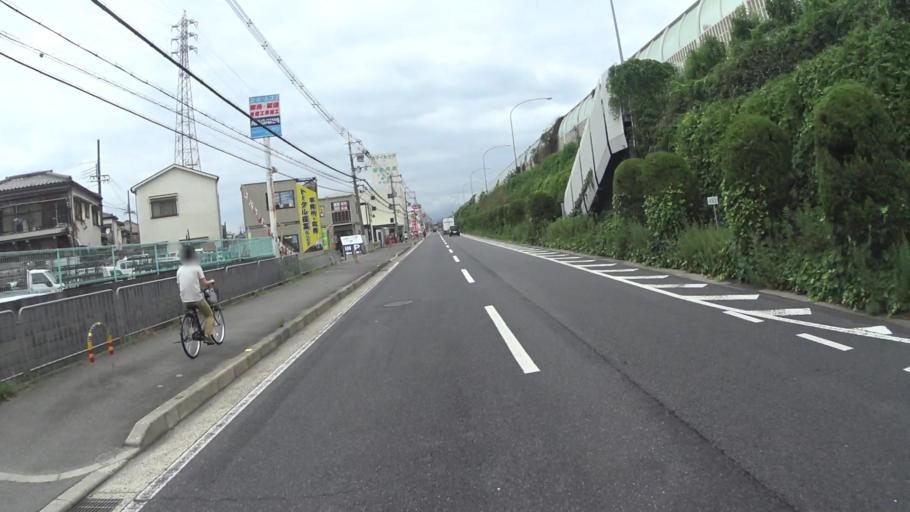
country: JP
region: Kyoto
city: Muko
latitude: 34.9221
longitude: 135.7099
